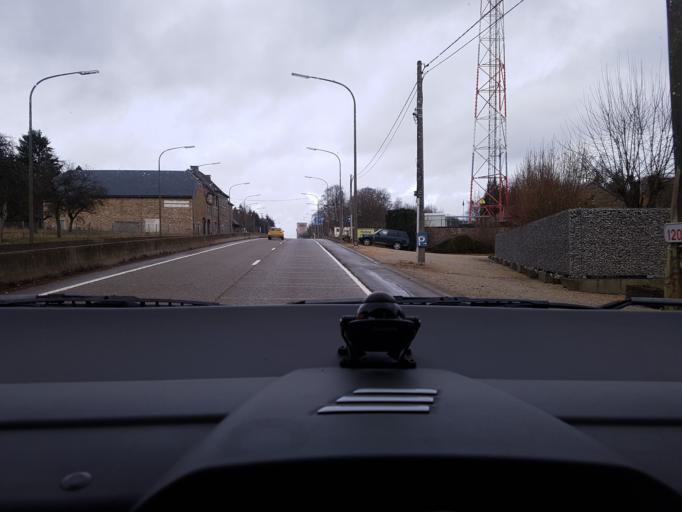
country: BE
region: Wallonia
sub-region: Province du Luxembourg
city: Tenneville
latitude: 50.1051
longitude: 5.4761
